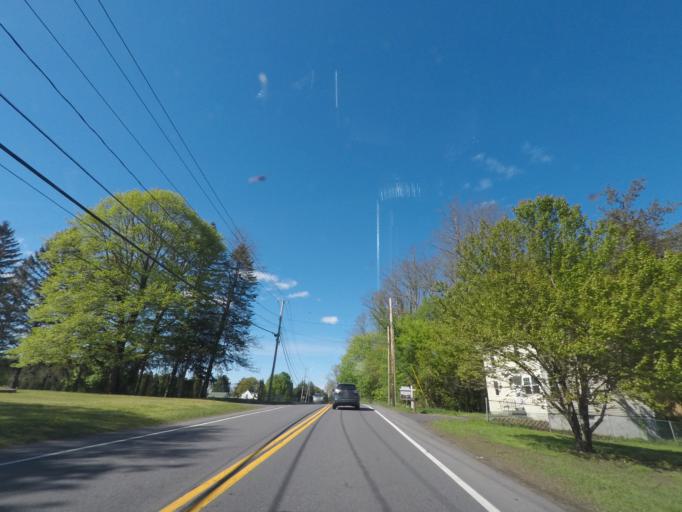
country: US
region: New York
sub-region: Albany County
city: Delmar
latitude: 42.5957
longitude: -73.7955
